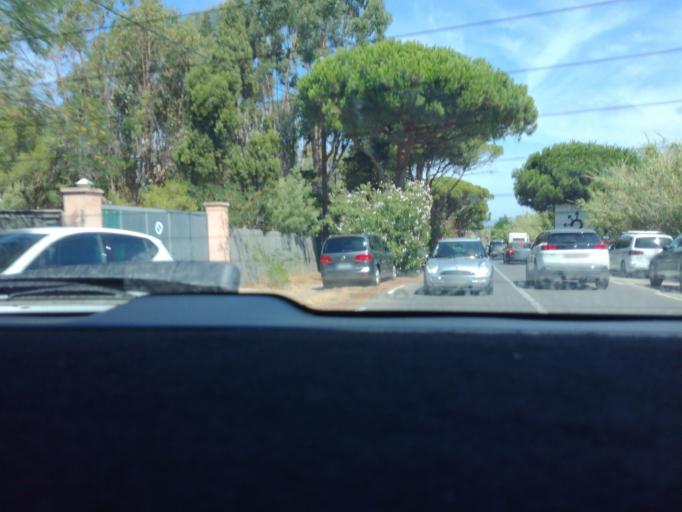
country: FR
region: Provence-Alpes-Cote d'Azur
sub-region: Departement du Var
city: Hyeres
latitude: 43.0386
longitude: 6.1449
